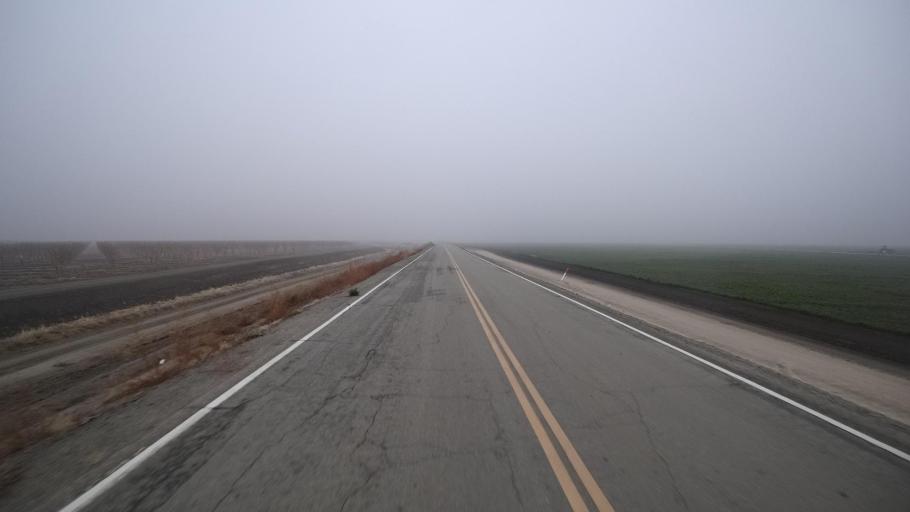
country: US
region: California
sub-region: Kern County
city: Buttonwillow
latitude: 35.4372
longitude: -119.5471
